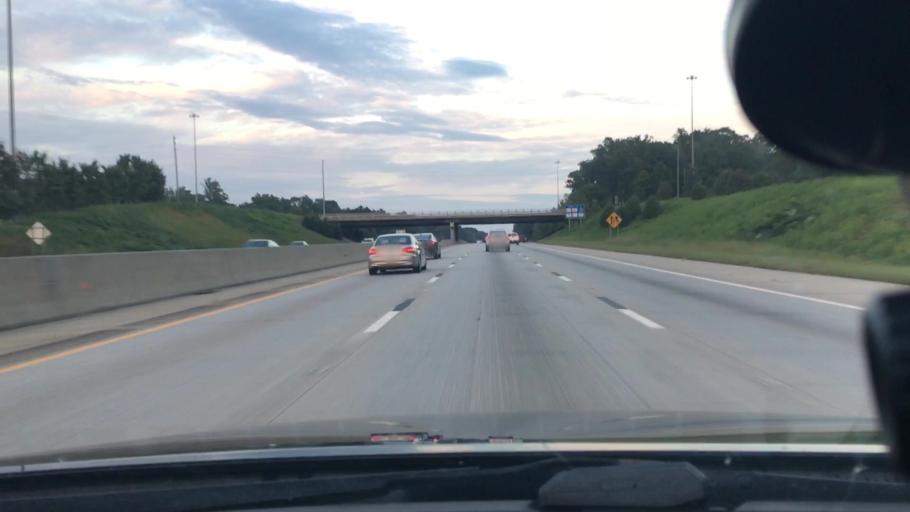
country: US
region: North Carolina
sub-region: Wake County
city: Cary
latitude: 35.7475
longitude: -78.7739
